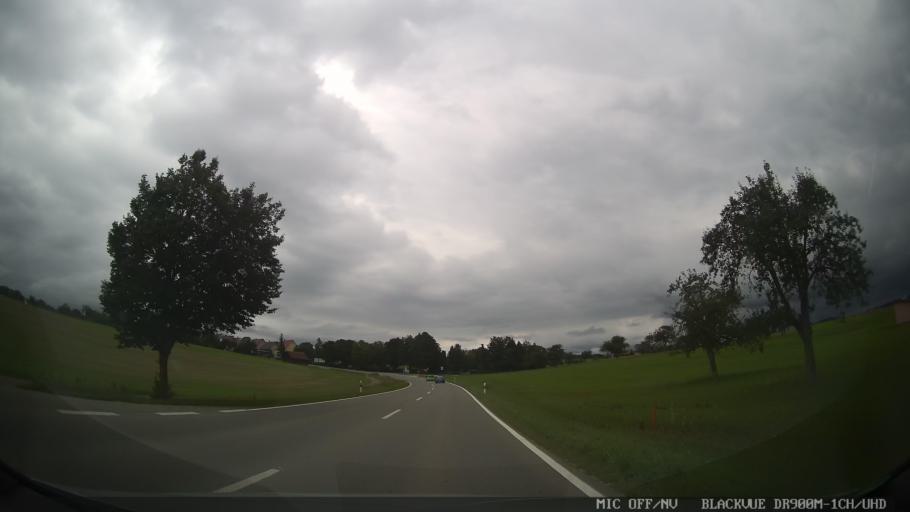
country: DE
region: Baden-Wuerttemberg
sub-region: Freiburg Region
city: Neuhausen ob Eck
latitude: 47.9779
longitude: 8.9267
